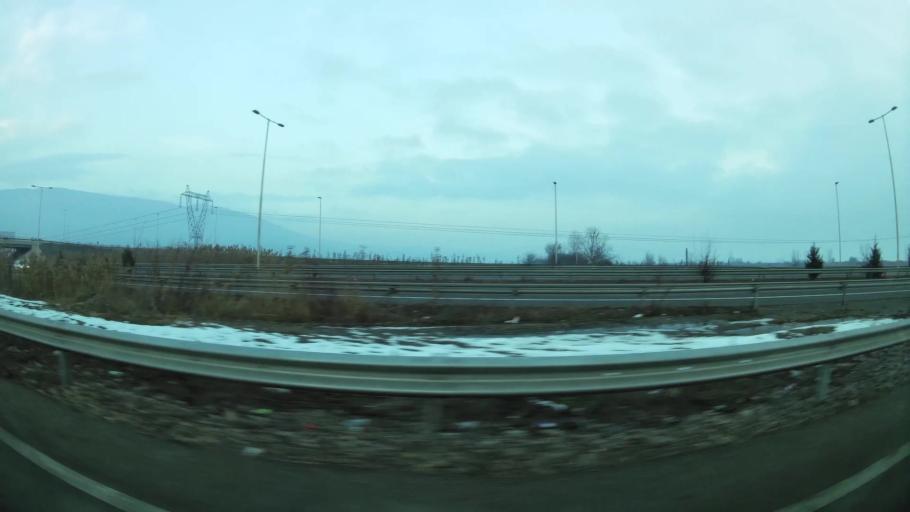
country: MK
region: Aracinovo
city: Arachinovo
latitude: 42.0170
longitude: 21.5338
